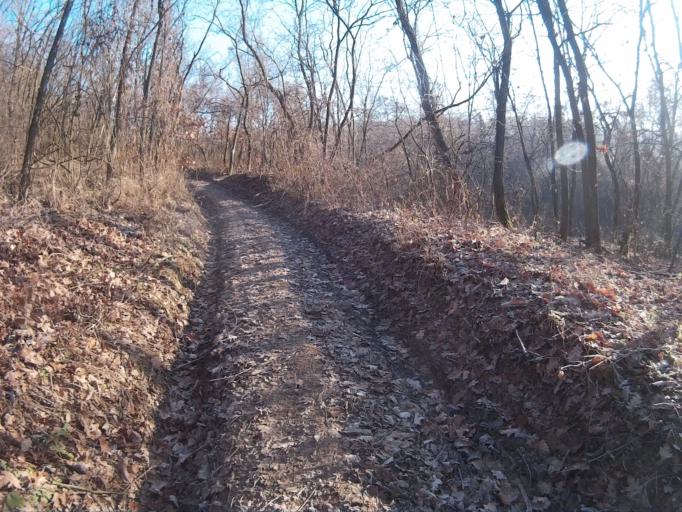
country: HU
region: Nograd
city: Bercel
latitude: 47.9101
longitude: 19.3885
